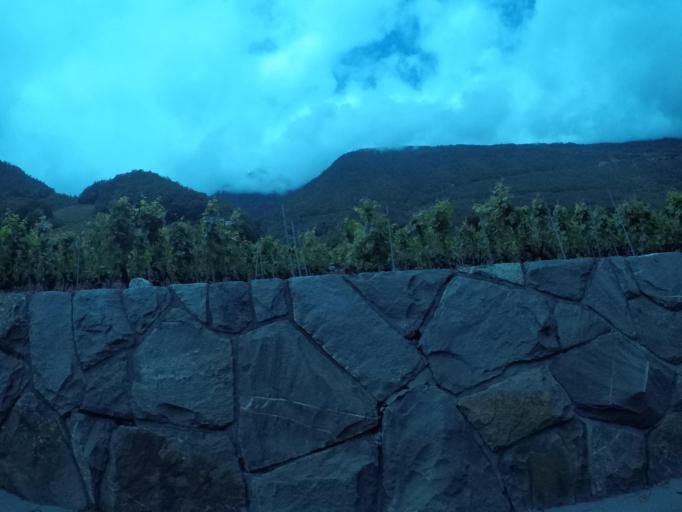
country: CH
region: Valais
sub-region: Martigny District
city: Martigny-Combe
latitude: 46.0792
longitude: 7.0535
